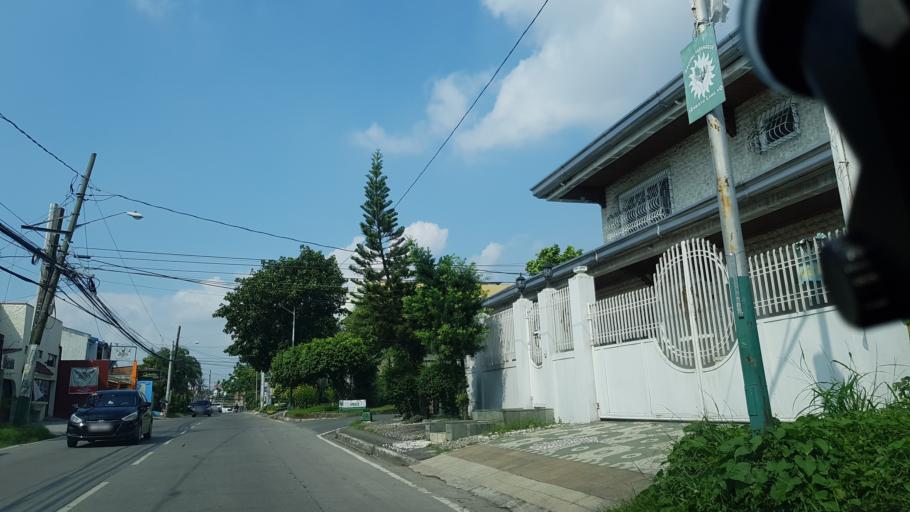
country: PH
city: Sambayanihan People's Village
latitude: 14.4823
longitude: 121.0308
